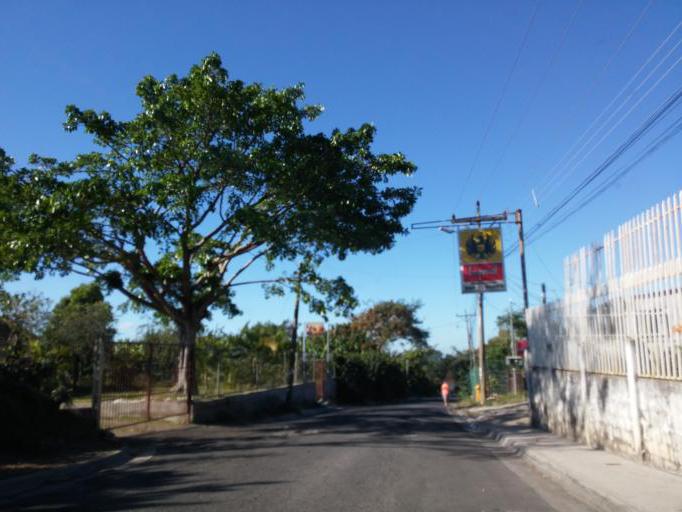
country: CR
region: Alajuela
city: Sabanilla
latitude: 10.0744
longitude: -84.2001
